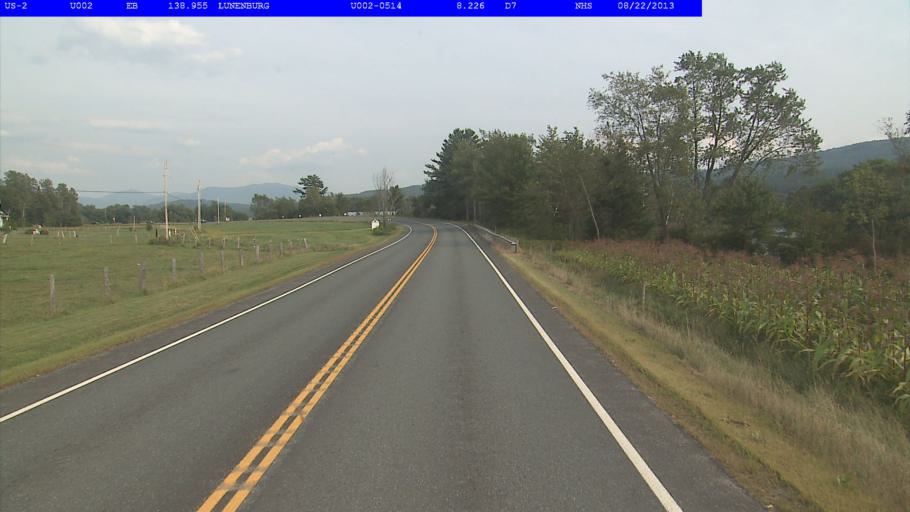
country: US
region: New Hampshire
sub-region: Coos County
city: Lancaster
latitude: 44.4844
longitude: -71.6264
